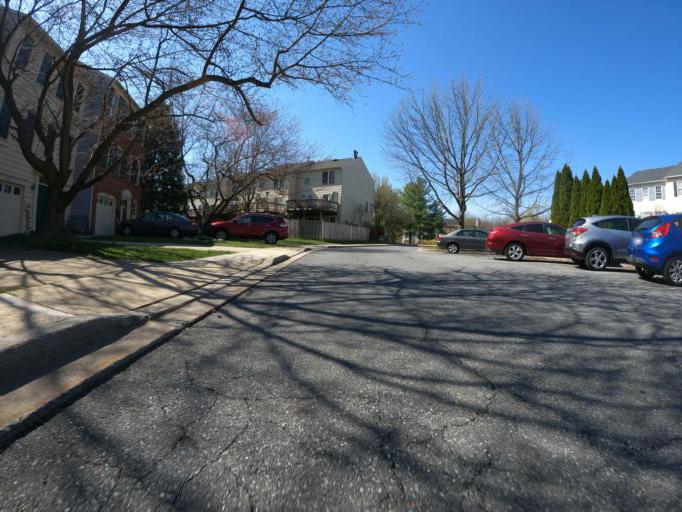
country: US
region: Maryland
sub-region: Frederick County
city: Ballenger Creek
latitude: 39.3760
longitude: -77.4289
